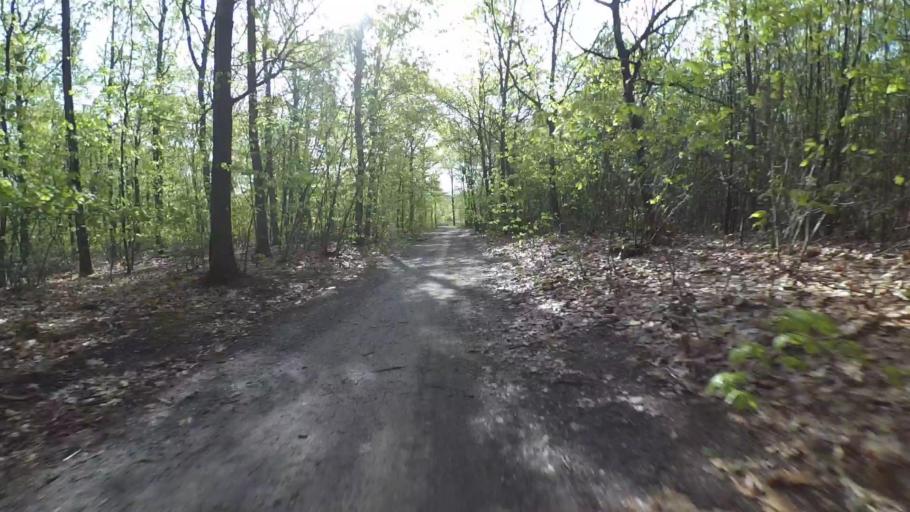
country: NL
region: Utrecht
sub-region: Gemeente Utrechtse Heuvelrug
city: Driebergen-Rijsenburg
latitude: 52.1003
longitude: 5.2925
